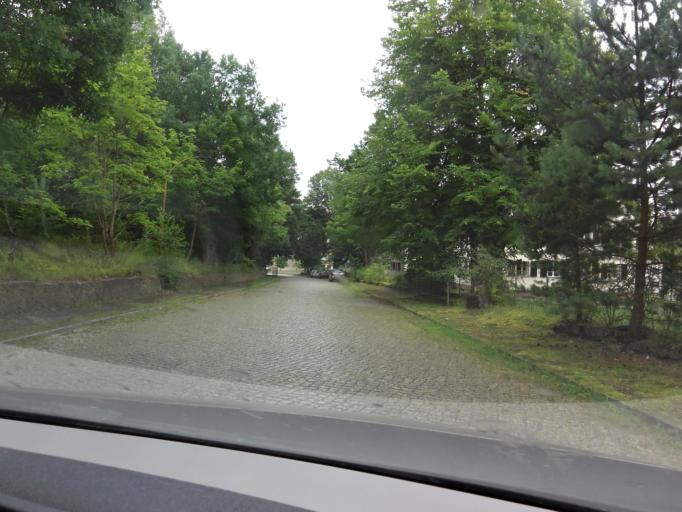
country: DE
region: Brandenburg
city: Furstenberg
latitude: 53.1921
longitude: 13.1601
